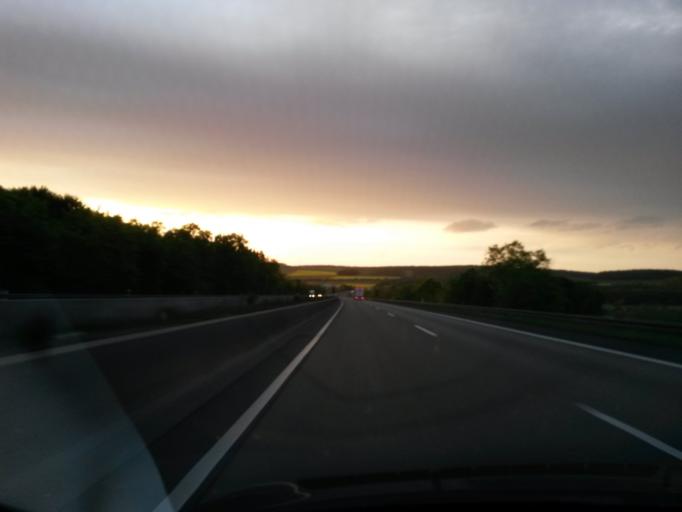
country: DE
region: Hesse
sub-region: Regierungsbezirk Kassel
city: Burghaun
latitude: 50.6509
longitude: 9.6816
